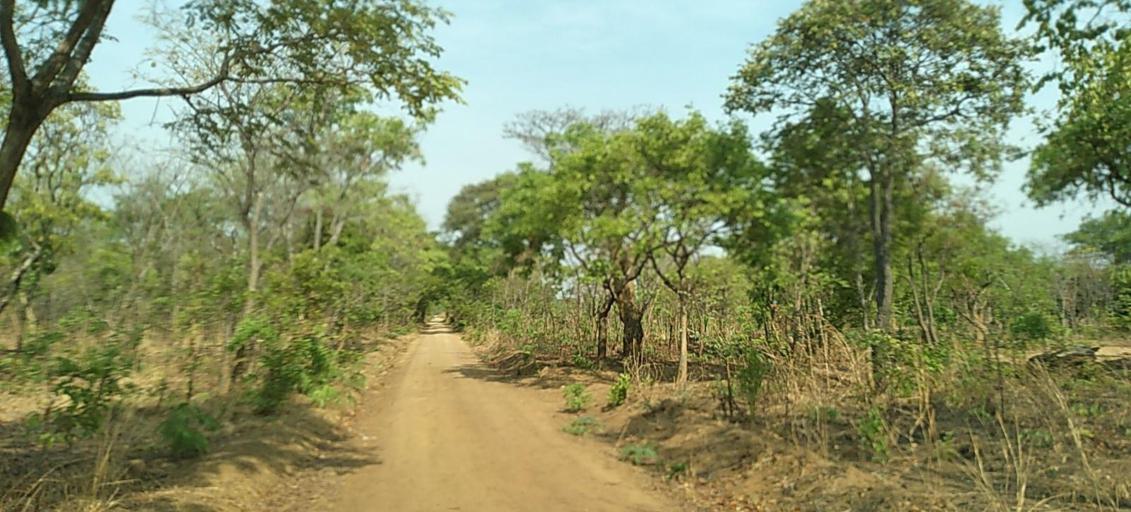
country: ZM
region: Copperbelt
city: Luanshya
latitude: -13.2201
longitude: 28.6623
